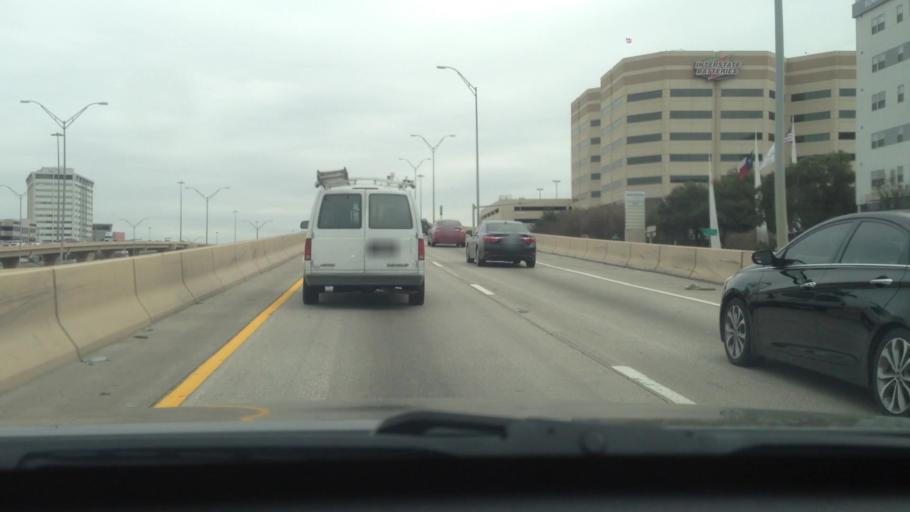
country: US
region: Texas
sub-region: Dallas County
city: Richardson
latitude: 32.9238
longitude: -96.7734
